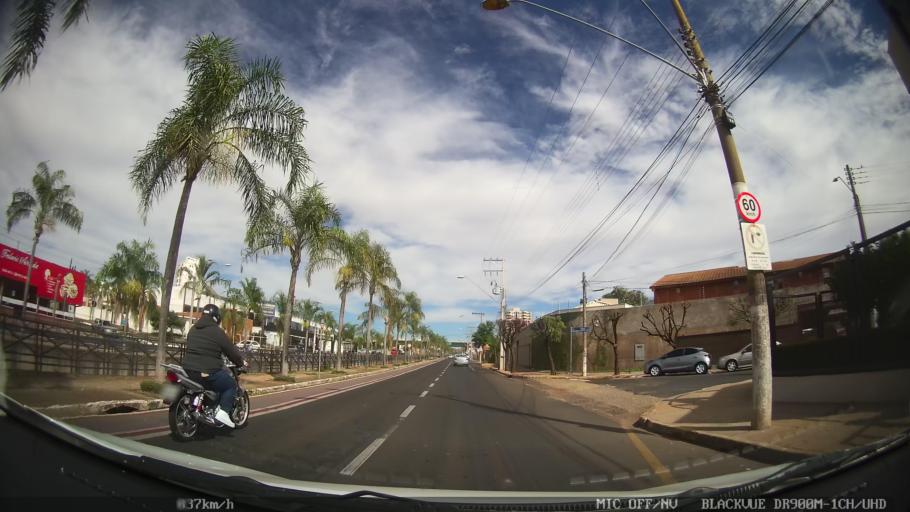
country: BR
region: Sao Paulo
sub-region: Catanduva
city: Catanduva
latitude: -21.1400
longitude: -48.9677
